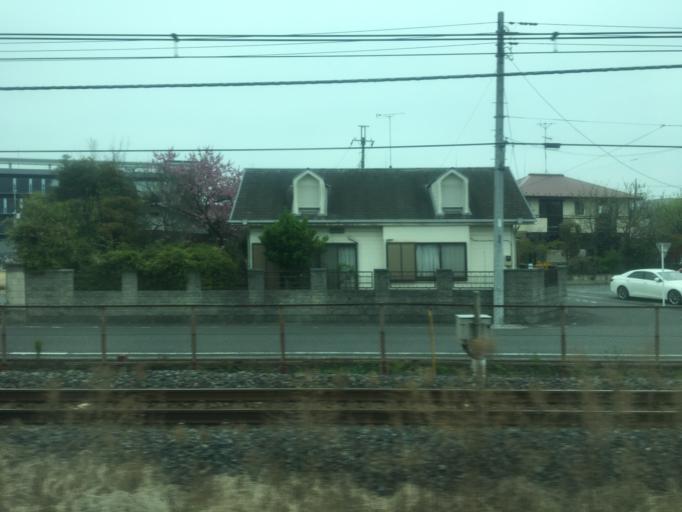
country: JP
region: Saitama
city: Fukiage-fujimi
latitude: 36.1127
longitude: 139.4333
